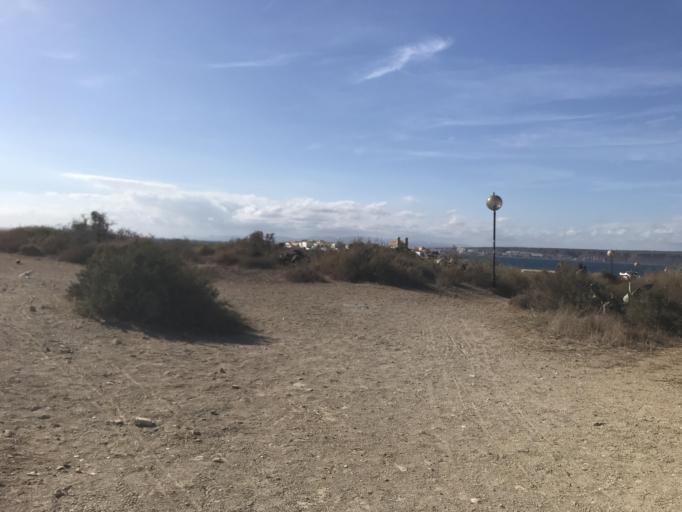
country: ES
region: Valencia
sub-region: Provincia de Alicante
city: Santa Pola
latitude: 38.1645
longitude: -0.4753
